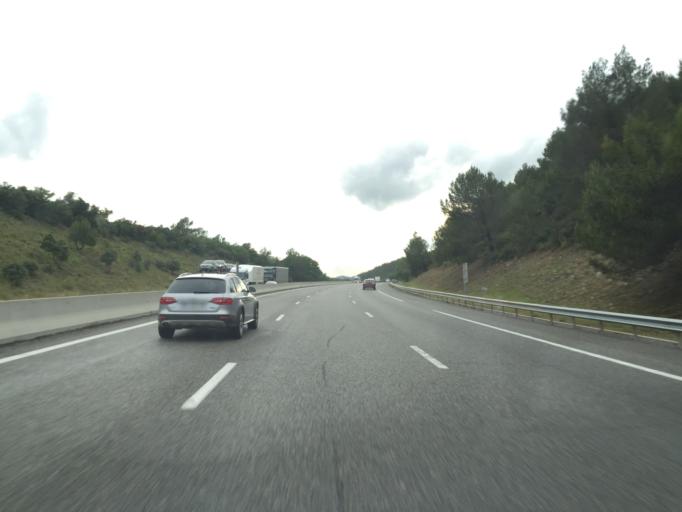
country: FR
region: Provence-Alpes-Cote d'Azur
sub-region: Departement du Var
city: Camps-la-Source
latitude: 43.4113
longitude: 6.1462
